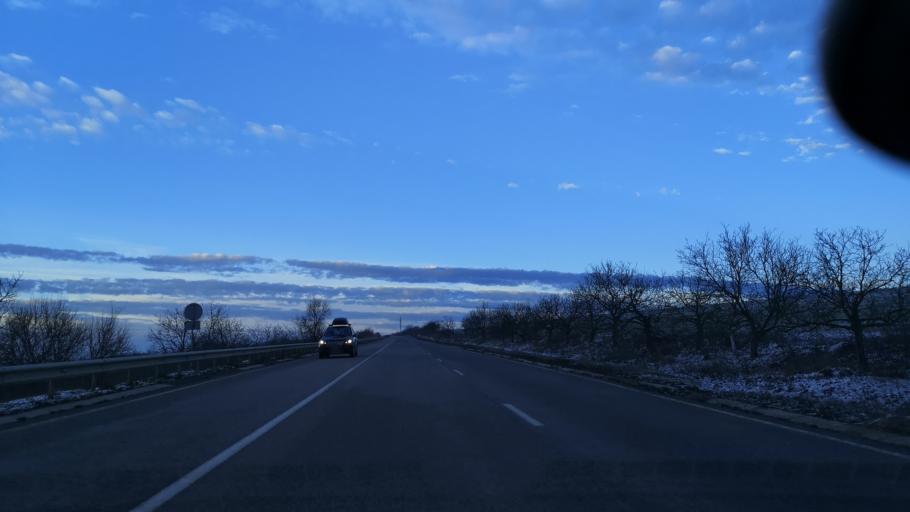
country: MD
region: Orhei
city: Orhei
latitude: 47.5271
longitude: 28.7960
